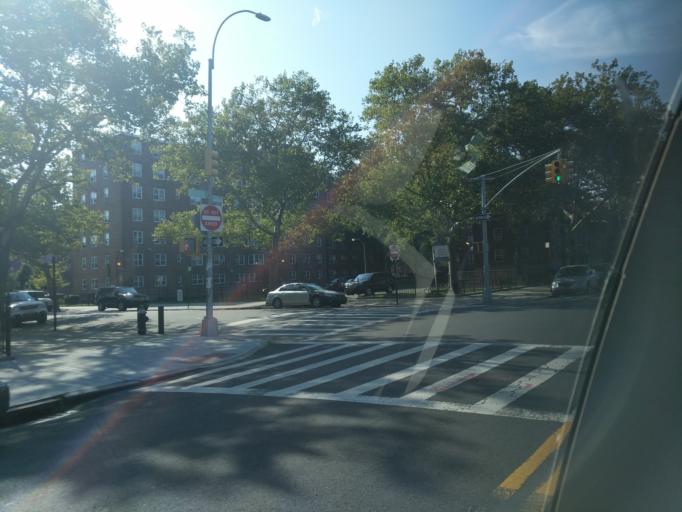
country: US
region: New York
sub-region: Queens County
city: Jamaica
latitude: 40.6940
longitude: -73.7920
